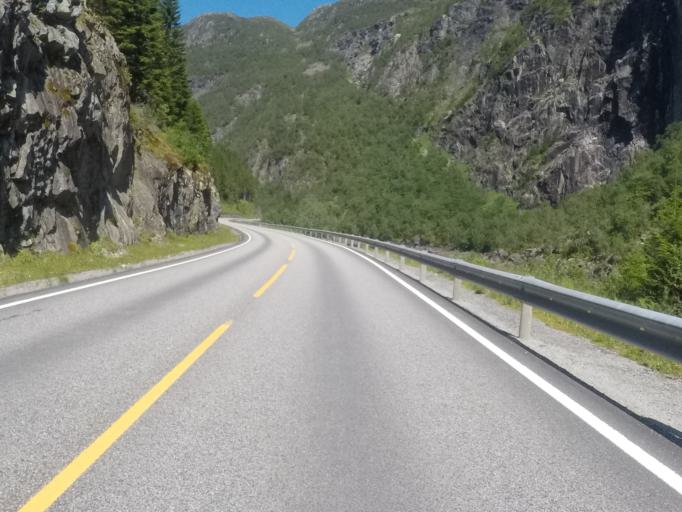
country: NO
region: Sogn og Fjordane
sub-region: Eid
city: Nordfjordeid
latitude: 61.9660
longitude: 6.1322
